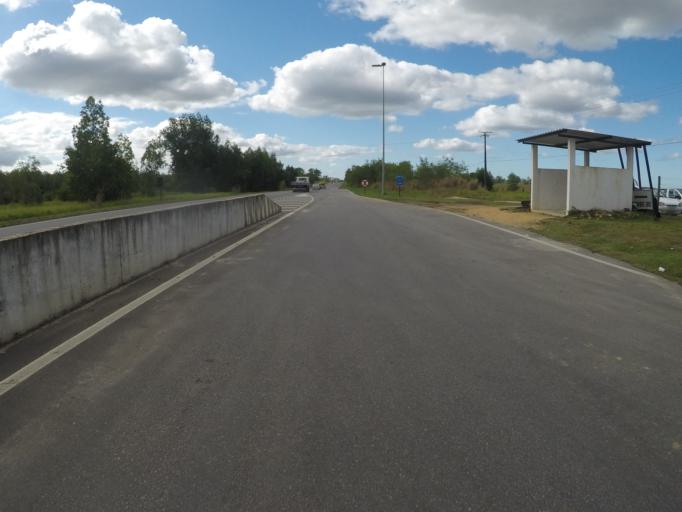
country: BR
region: Espirito Santo
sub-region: Linhares
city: Linhares
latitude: -19.1771
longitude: -40.0914
